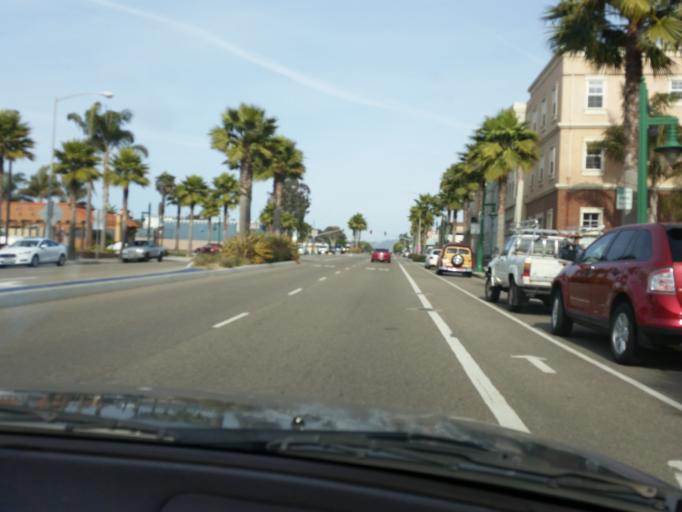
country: US
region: California
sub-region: San Luis Obispo County
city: Grover Beach
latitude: 35.1219
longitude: -120.6288
